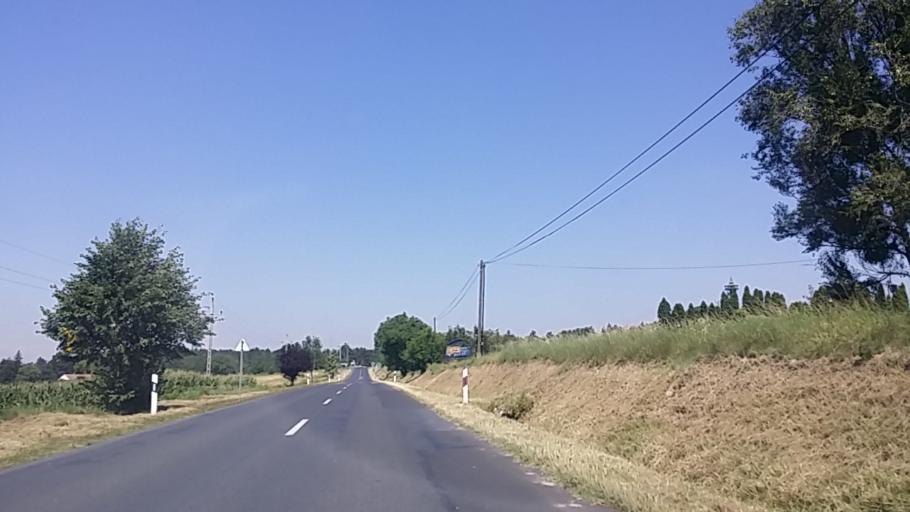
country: HU
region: Zala
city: Cserszegtomaj
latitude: 46.7944
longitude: 17.2094
